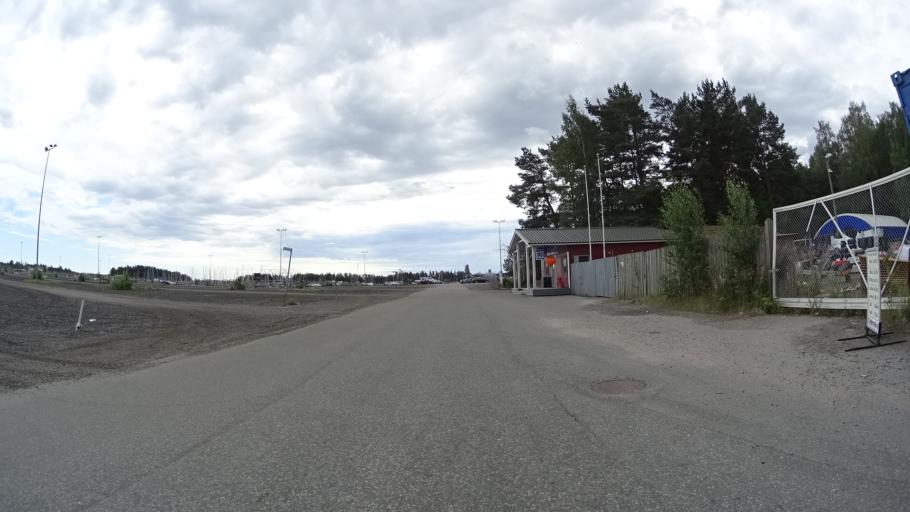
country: FI
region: Uusimaa
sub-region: Helsinki
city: Koukkuniemi
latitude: 60.1470
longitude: 24.7138
